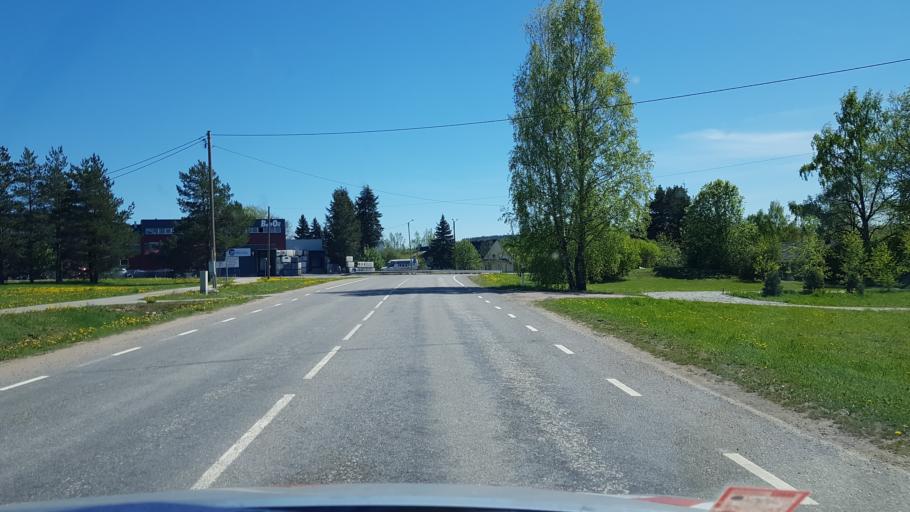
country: EE
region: Tartu
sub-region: UElenurme vald
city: Ulenurme
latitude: 58.3010
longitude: 26.8654
